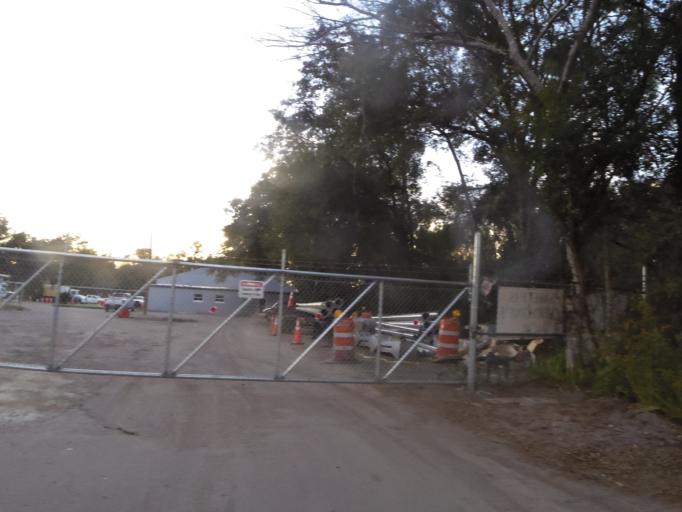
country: US
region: Florida
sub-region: Duval County
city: Jacksonville
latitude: 30.2755
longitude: -81.6370
